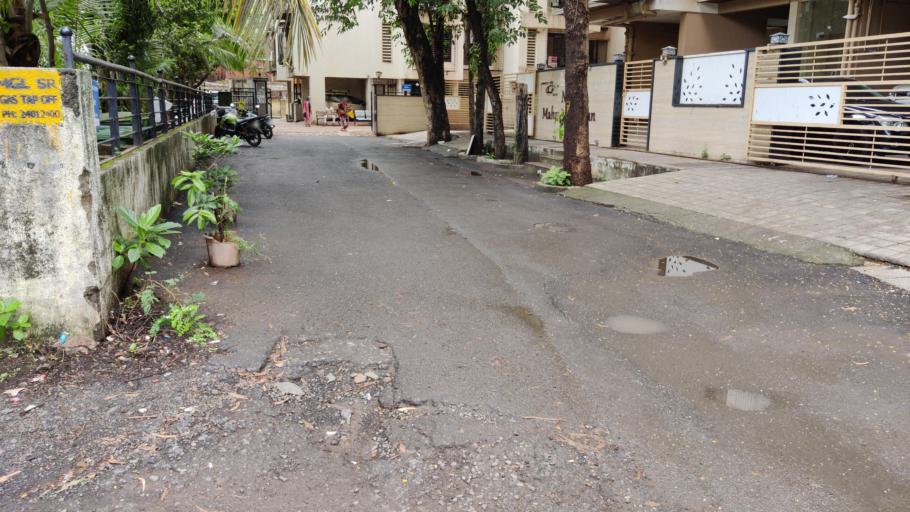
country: IN
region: Maharashtra
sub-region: Mumbai Suburban
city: Borivli
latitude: 19.2469
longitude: 72.8599
